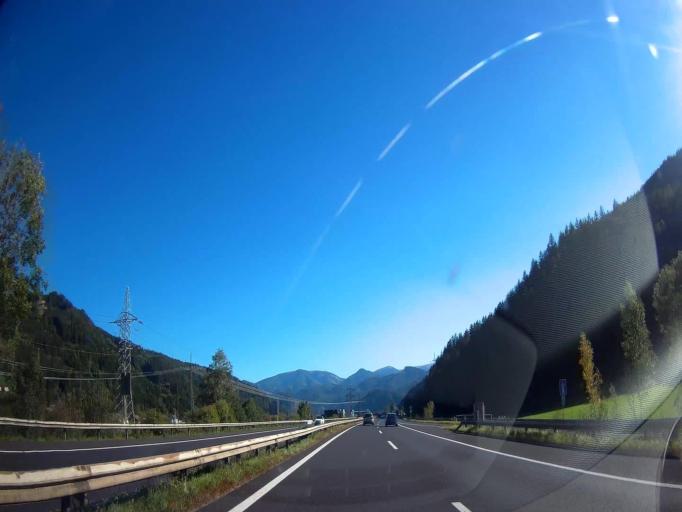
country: AT
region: Styria
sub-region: Politischer Bezirk Leoben
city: Traboch
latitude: 47.3642
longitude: 14.9971
